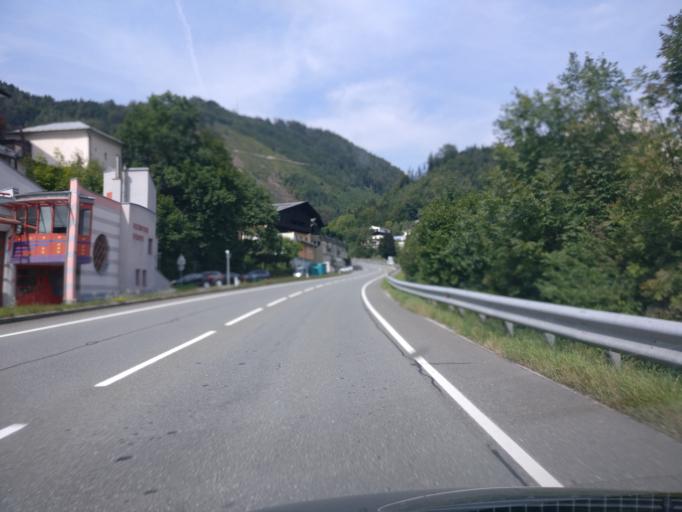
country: AT
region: Salzburg
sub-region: Politischer Bezirk Sankt Johann im Pongau
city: Werfen
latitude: 47.4777
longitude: 13.1892
